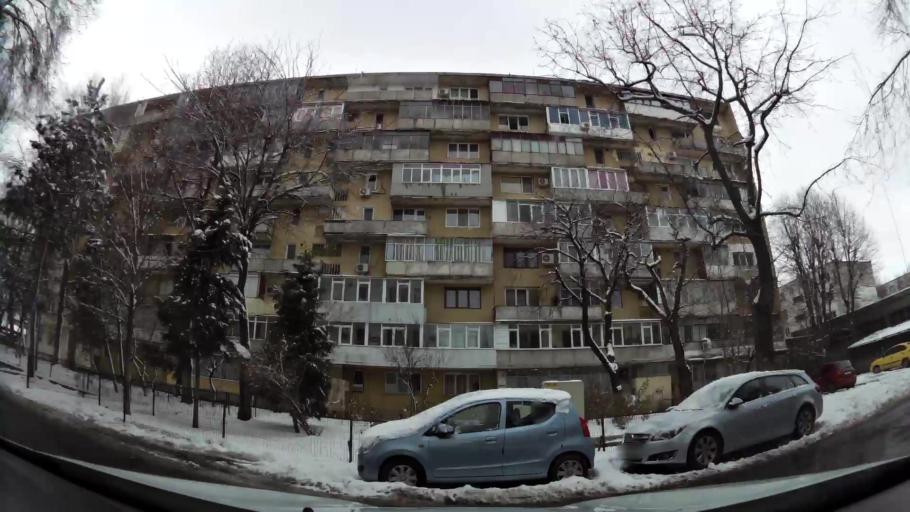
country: RO
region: Bucuresti
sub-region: Municipiul Bucuresti
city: Bucuresti
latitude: 44.3883
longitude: 26.1121
